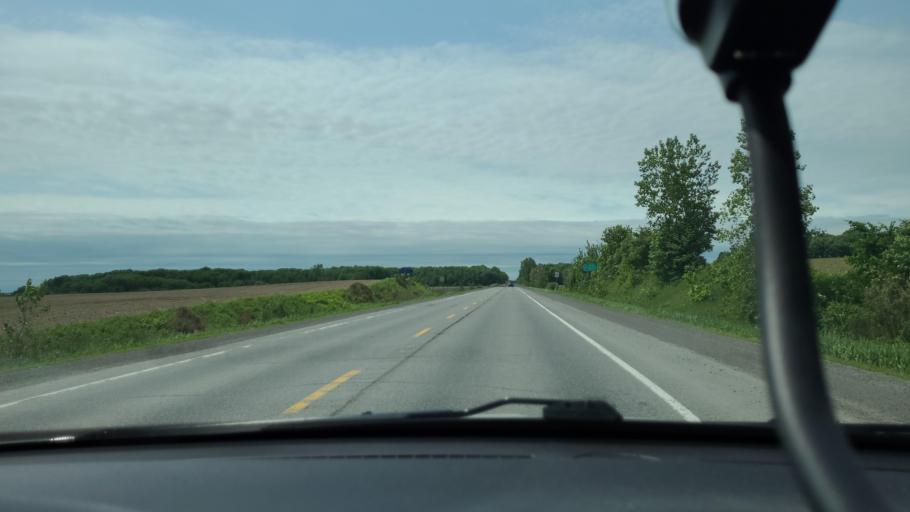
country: CA
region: Quebec
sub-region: Lanaudiere
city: Saint-Jacques
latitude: 45.9507
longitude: -73.5839
